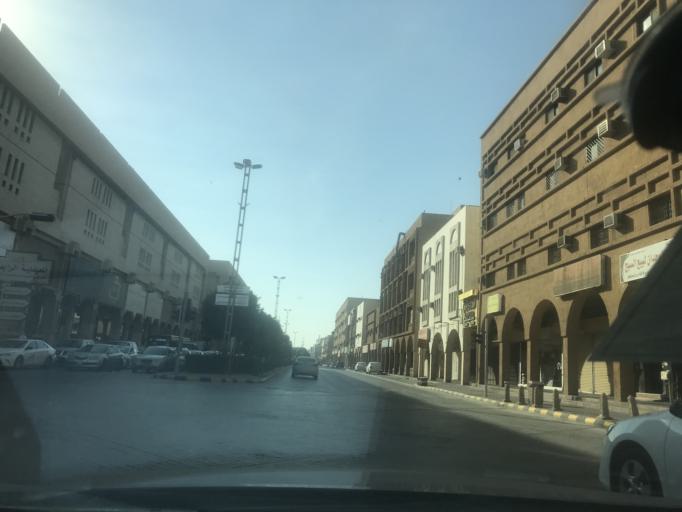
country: SA
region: Ar Riyad
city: Riyadh
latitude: 24.6315
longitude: 46.7098
